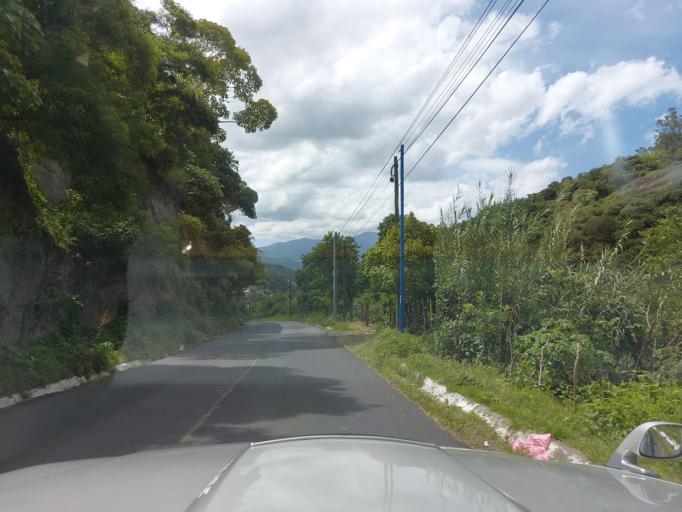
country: GT
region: Sacatepequez
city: Pastores
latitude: 14.6068
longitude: -90.7670
